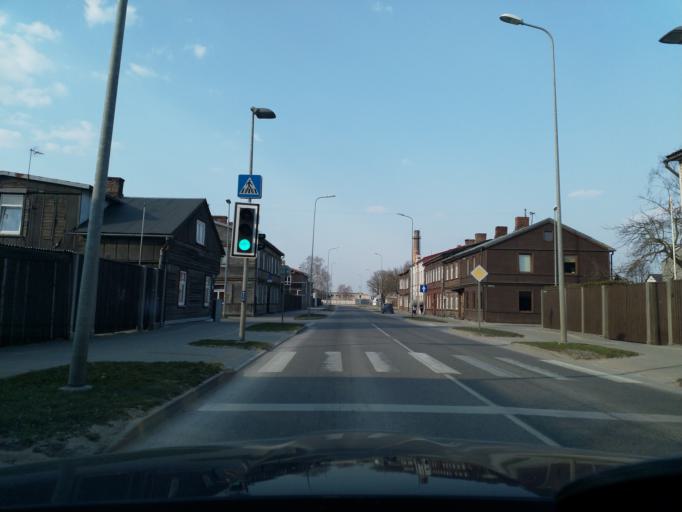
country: LV
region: Liepaja
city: Liepaja
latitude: 56.5076
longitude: 21.0253
